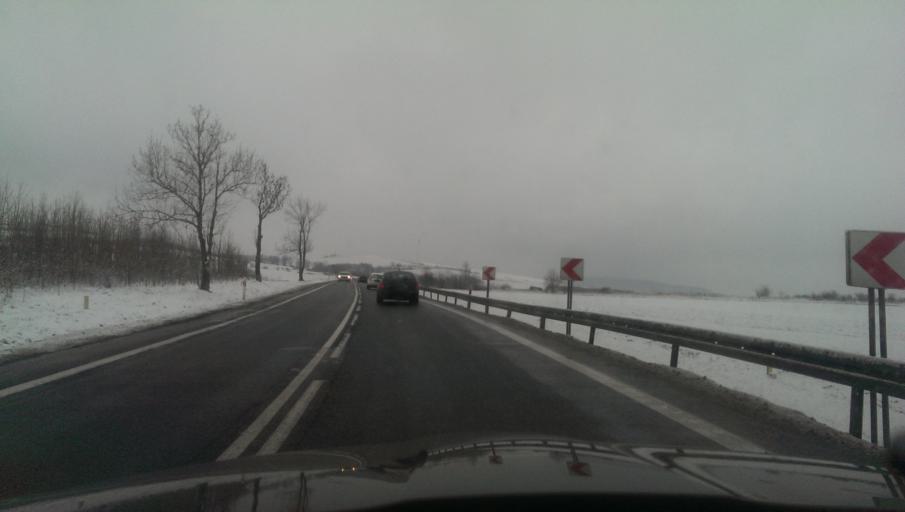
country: PL
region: Subcarpathian Voivodeship
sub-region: Powiat krosnienski
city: Rymanow
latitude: 49.5729
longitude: 21.8846
